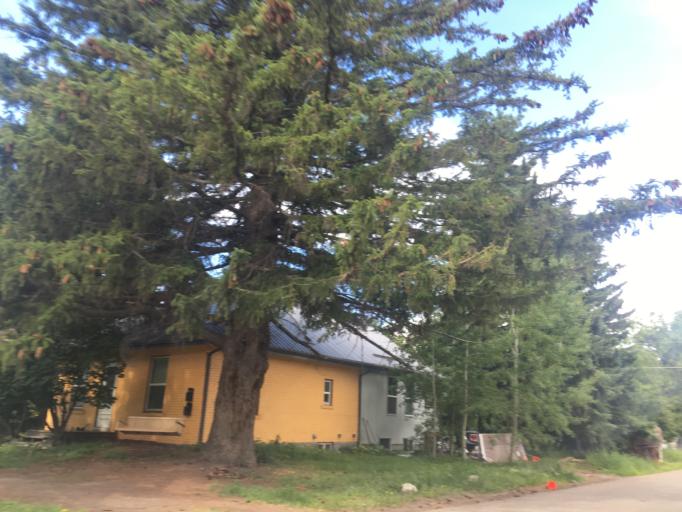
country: US
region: Montana
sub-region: Gallatin County
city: Bozeman
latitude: 45.6839
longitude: -111.0244
